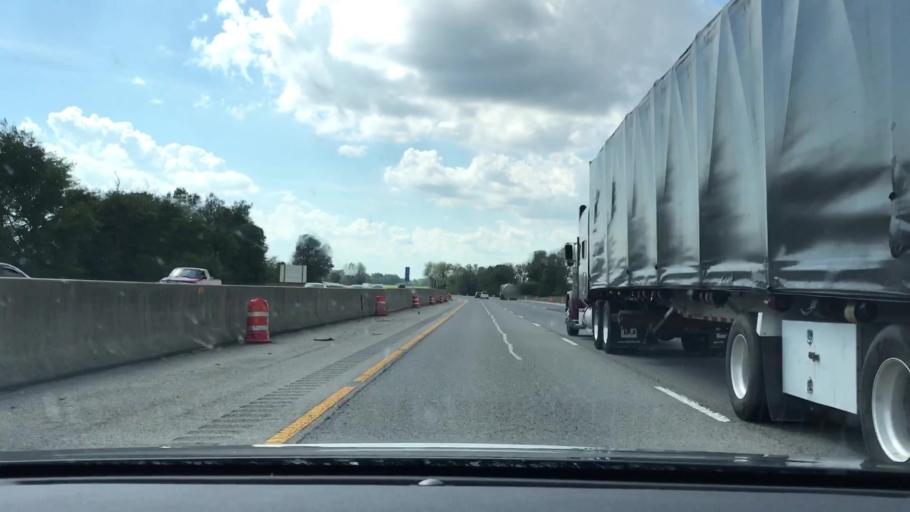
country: US
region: Kentucky
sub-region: Edmonson County
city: Brownsville
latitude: 37.0377
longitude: -86.2319
